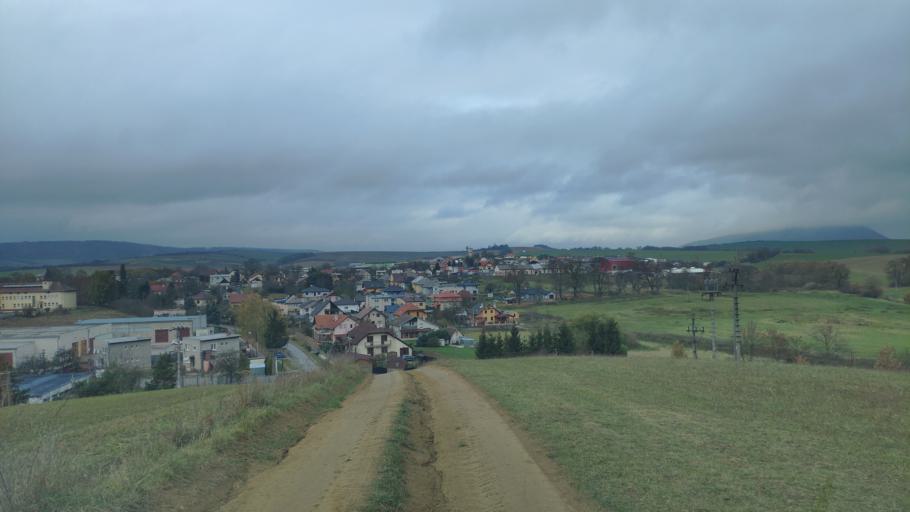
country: SK
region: Presovsky
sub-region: Okres Presov
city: Presov
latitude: 49.0108
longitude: 21.1921
